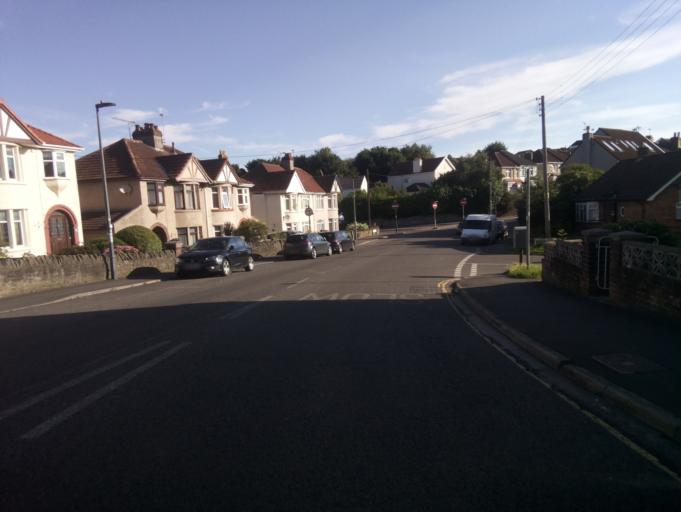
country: GB
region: England
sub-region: South Gloucestershire
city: Kingswood
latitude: 51.4497
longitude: -2.5163
